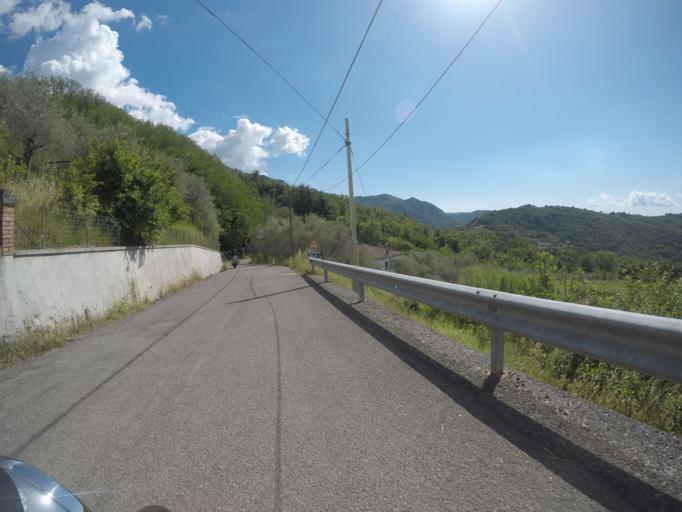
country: IT
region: Tuscany
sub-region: Provincia di Massa-Carrara
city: Casola in Lunigiana
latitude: 44.1808
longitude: 10.1561
